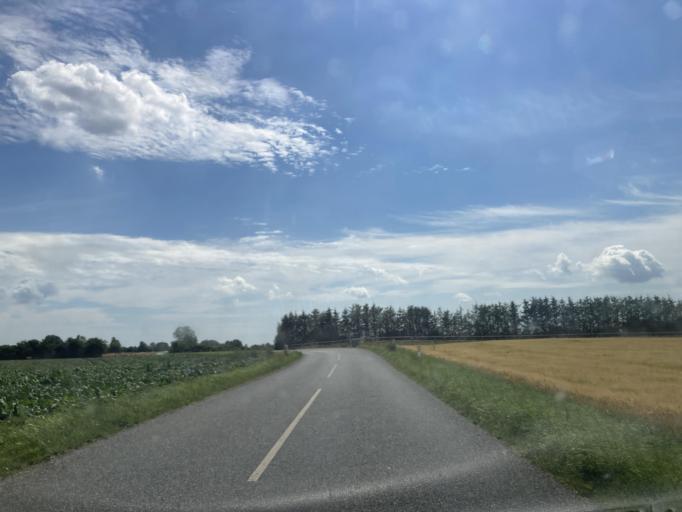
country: DK
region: Zealand
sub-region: Faxe Kommune
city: Haslev
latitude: 55.4030
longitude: 11.9338
